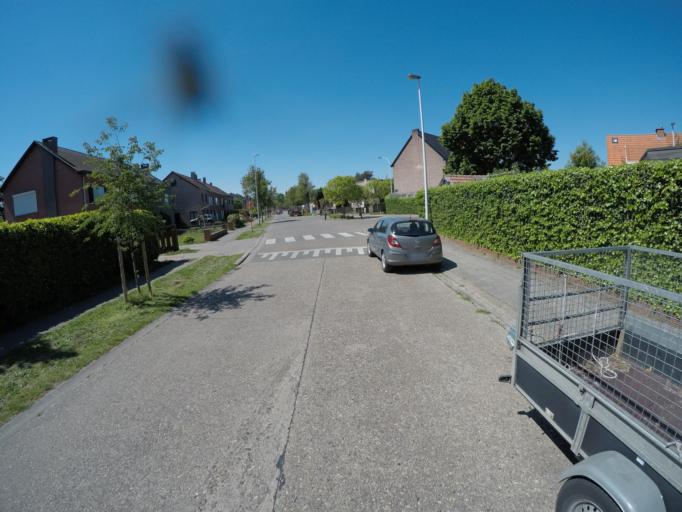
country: BE
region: Flanders
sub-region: Provincie Antwerpen
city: Schoten
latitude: 51.2478
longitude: 4.5120
